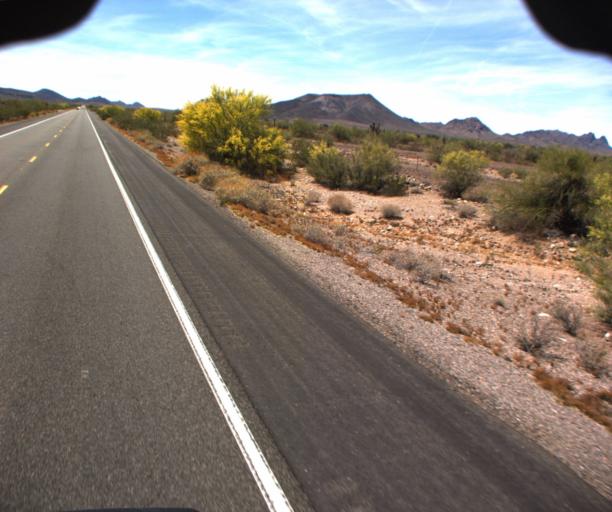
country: US
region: Arizona
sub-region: La Paz County
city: Quartzsite
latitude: 33.6732
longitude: -113.9709
